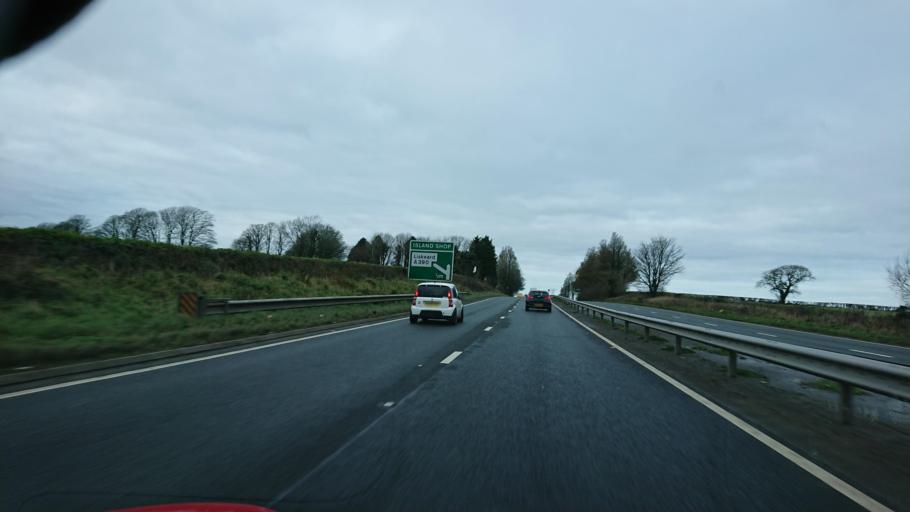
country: GB
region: England
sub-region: Cornwall
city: Liskeard
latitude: 50.4409
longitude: -4.4434
